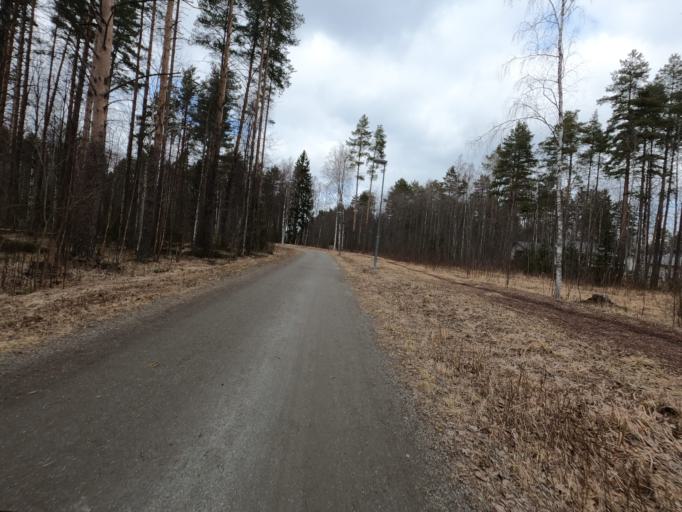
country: FI
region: North Karelia
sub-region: Joensuu
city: Joensuu
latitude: 62.5726
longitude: 29.8125
